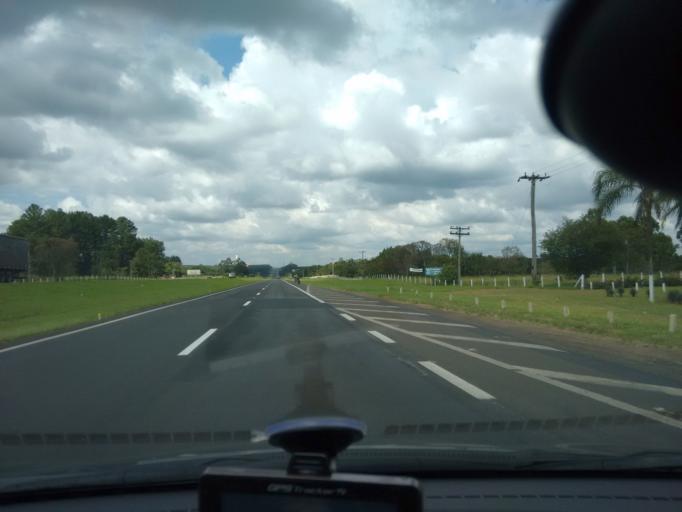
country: BR
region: Sao Paulo
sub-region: Sao Carlos
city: Sao Carlos
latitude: -22.0960
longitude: -47.8293
